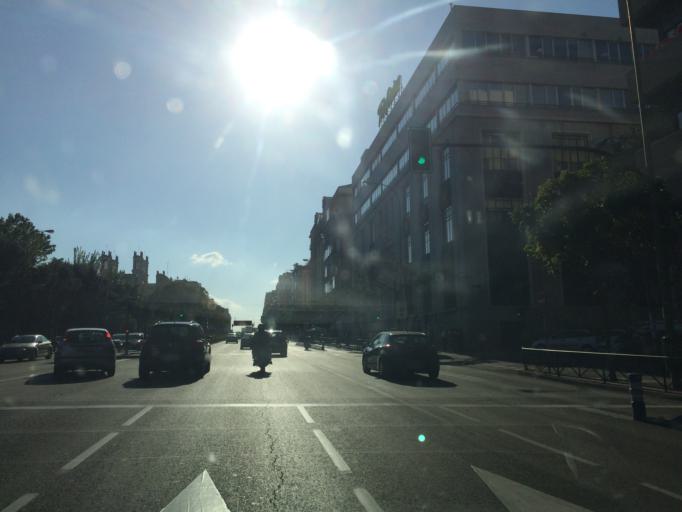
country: ES
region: Madrid
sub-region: Provincia de Madrid
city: Chamberi
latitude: 40.4467
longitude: -3.6983
